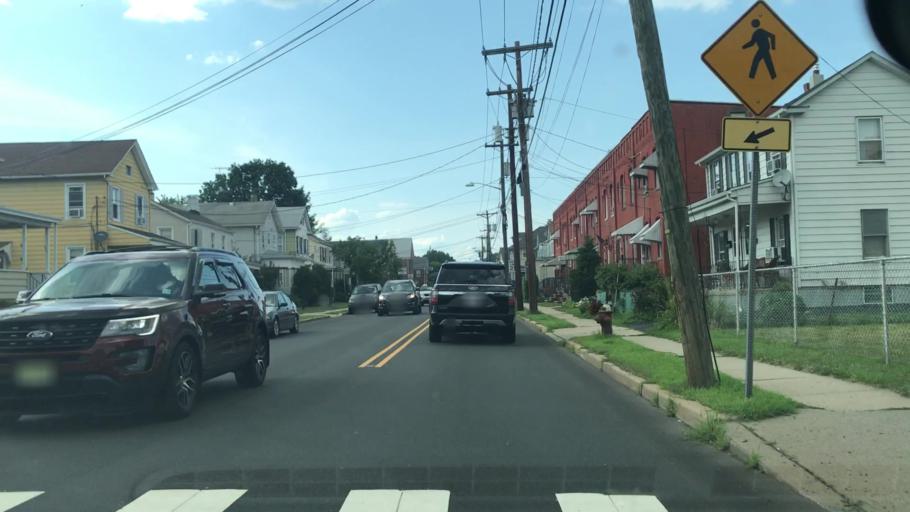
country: US
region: New Jersey
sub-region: Somerset County
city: Raritan
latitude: 40.5674
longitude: -74.6378
